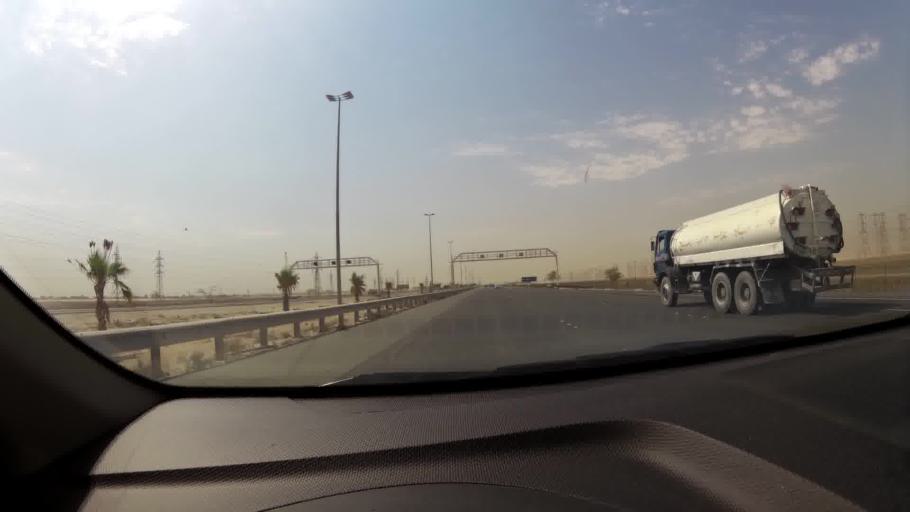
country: KW
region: Al Ahmadi
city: Al Fahahil
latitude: 28.8183
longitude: 48.2609
